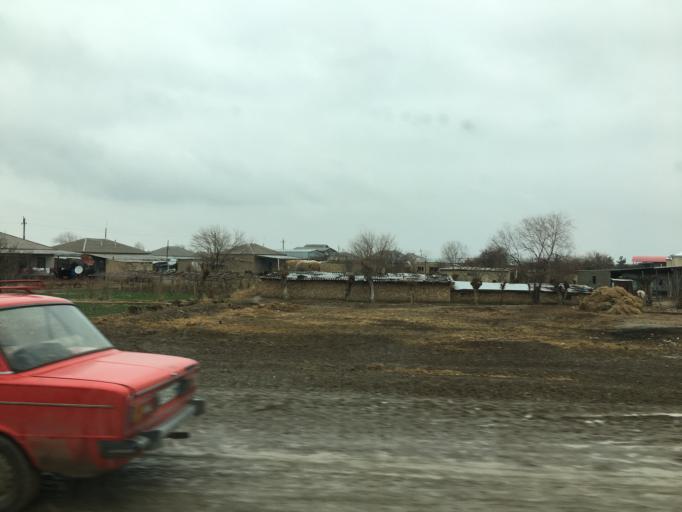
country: TM
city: Murgab
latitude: 37.4701
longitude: 62.0296
